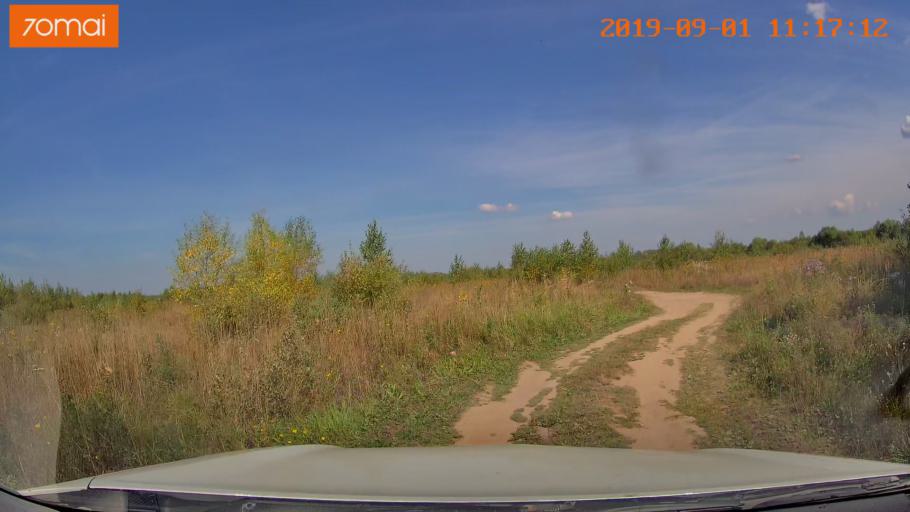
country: RU
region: Kaluga
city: Detchino
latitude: 54.8246
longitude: 36.3672
